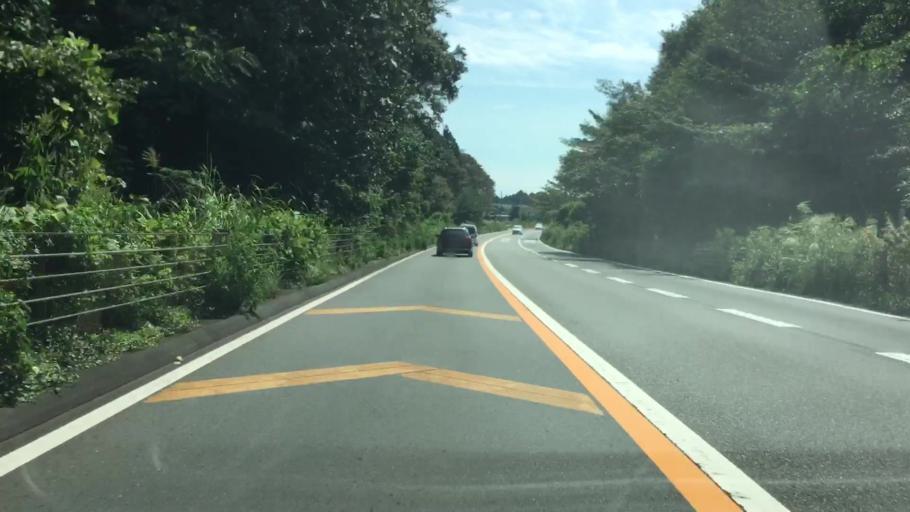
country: JP
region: Shizuoka
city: Fujinomiya
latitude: 35.2881
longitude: 138.6110
